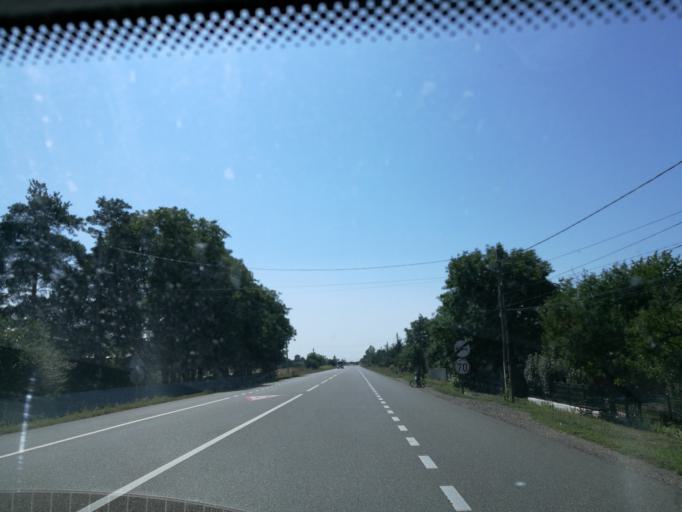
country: RO
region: Bacau
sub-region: Comuna Filipesti
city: Filipesti
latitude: 46.7910
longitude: 26.8891
